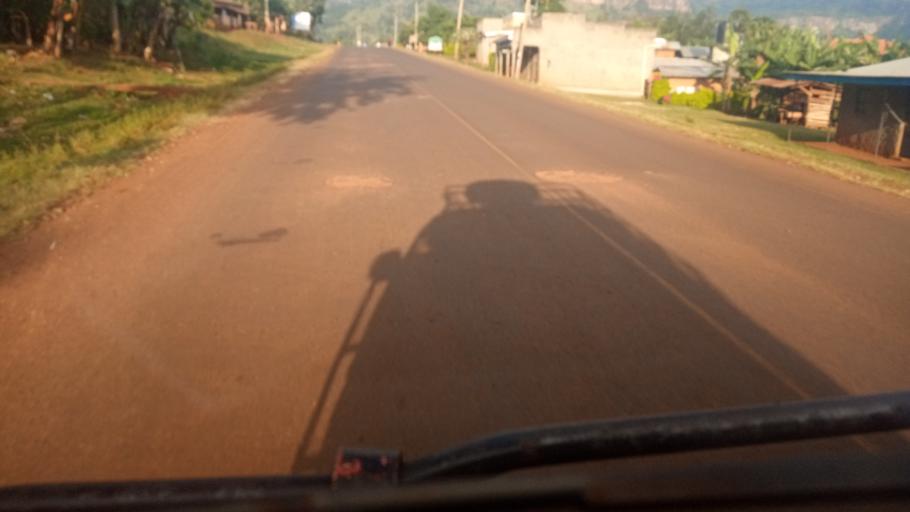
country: UG
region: Eastern Region
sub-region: Kapchorwa District
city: Kapchorwa
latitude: 1.3239
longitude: 34.3516
